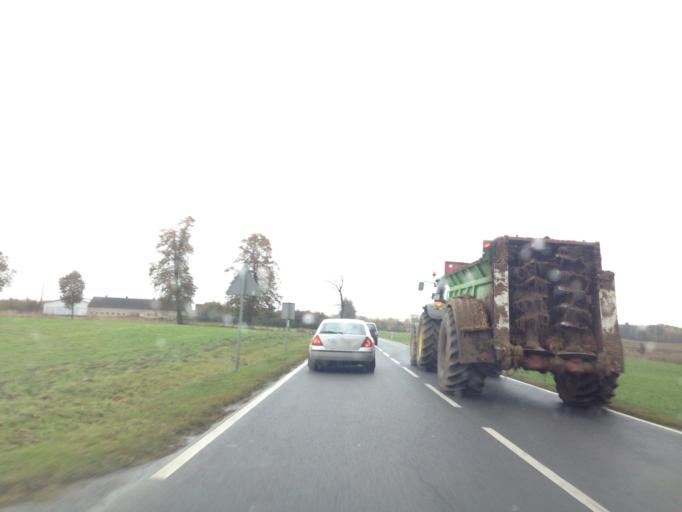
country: PL
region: Warmian-Masurian Voivodeship
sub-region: Powiat nowomiejski
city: Biskupiec
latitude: 53.6004
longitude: 19.4127
